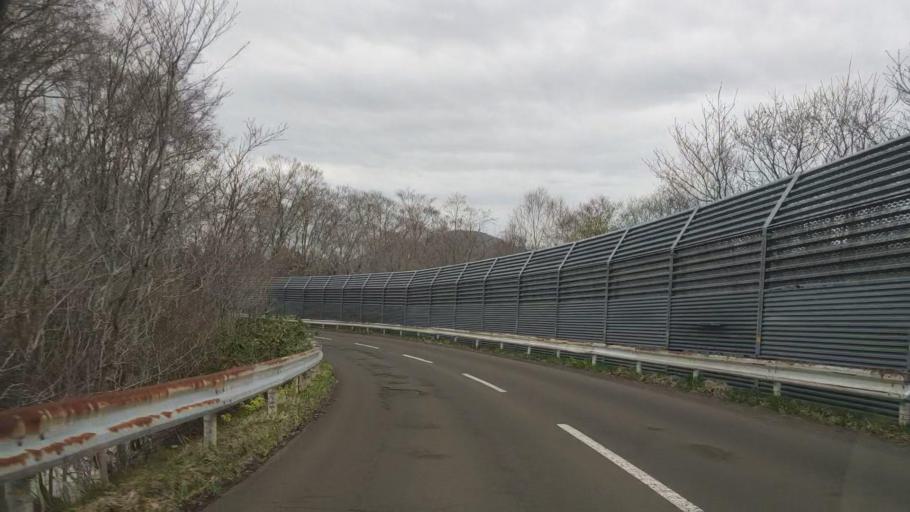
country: JP
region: Akita
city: Hanawa
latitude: 40.4188
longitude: 140.8216
